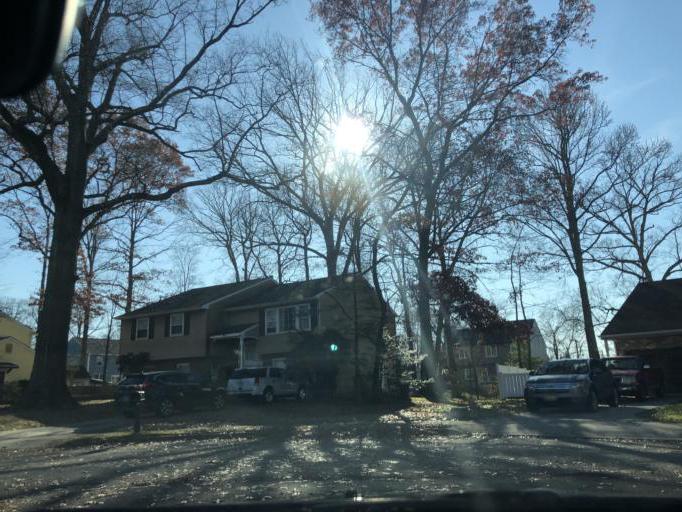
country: US
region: New Jersey
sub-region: Burlington County
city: Moorestown-Lenola
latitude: 39.9640
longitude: -74.9780
